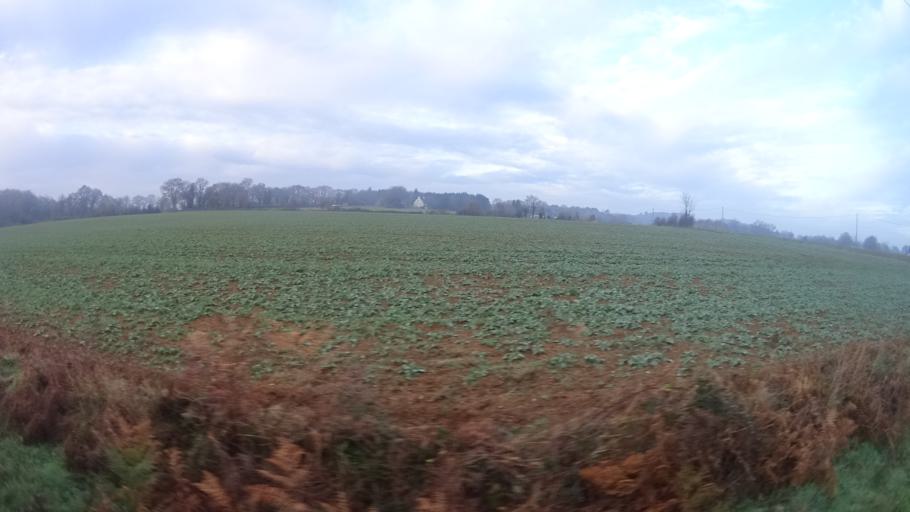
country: FR
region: Pays de la Loire
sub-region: Departement de la Loire-Atlantique
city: Avessac
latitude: 47.6478
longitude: -2.0243
